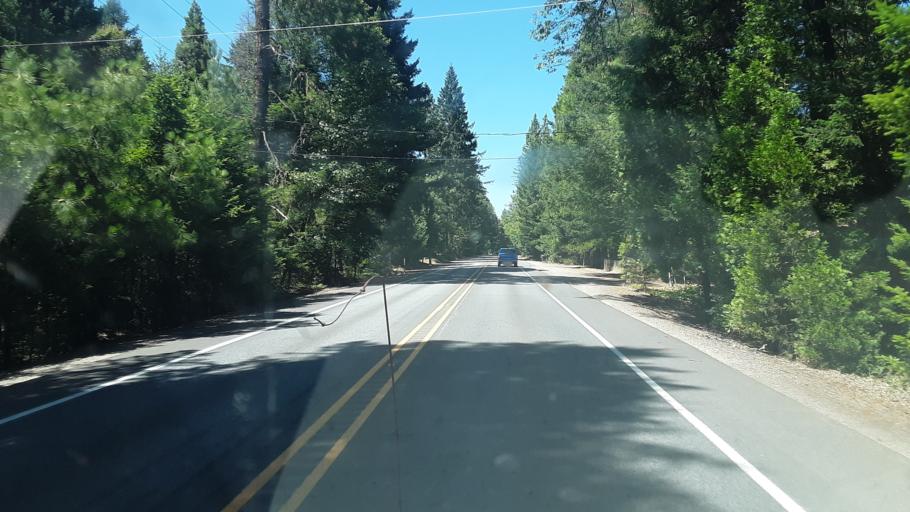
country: US
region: Oregon
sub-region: Josephine County
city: Cave Junction
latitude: 42.3014
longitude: -123.6115
